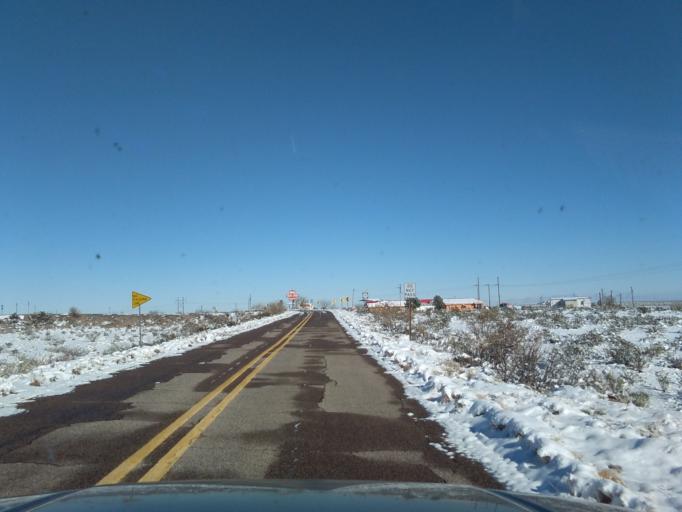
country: US
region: New Mexico
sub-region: Socorro County
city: Socorro
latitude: 33.6349
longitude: -107.1216
